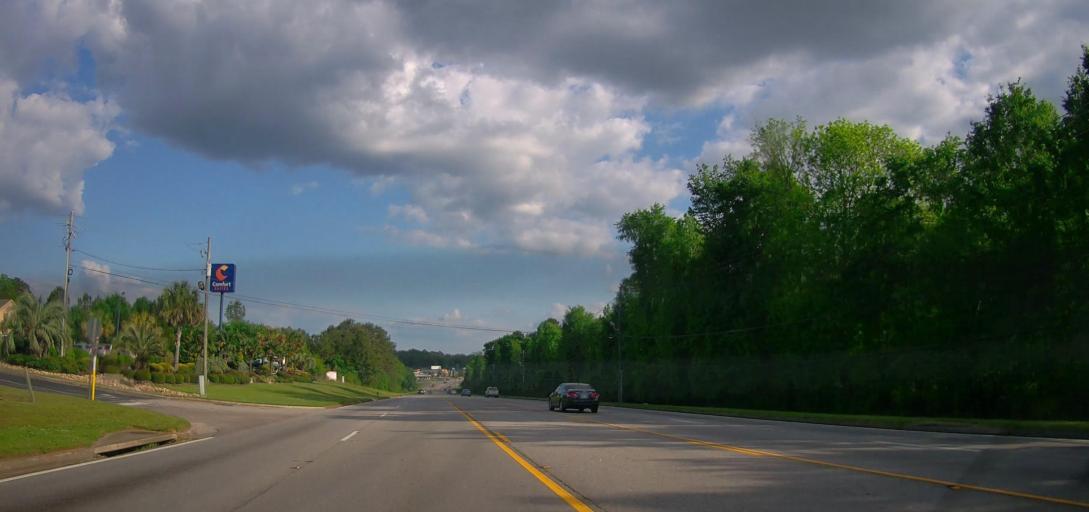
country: US
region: Georgia
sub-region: Baldwin County
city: Milledgeville
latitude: 33.1242
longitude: -83.2642
